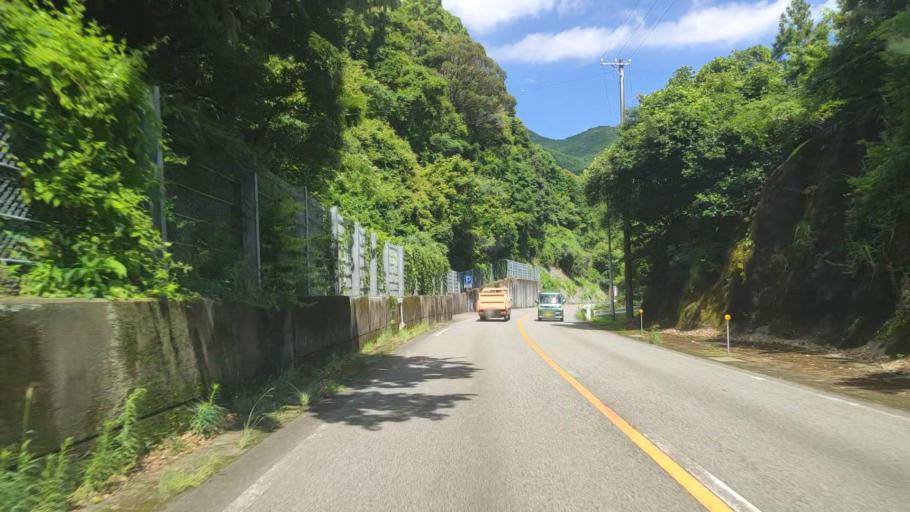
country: JP
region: Mie
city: Owase
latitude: 33.9182
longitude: 136.1098
